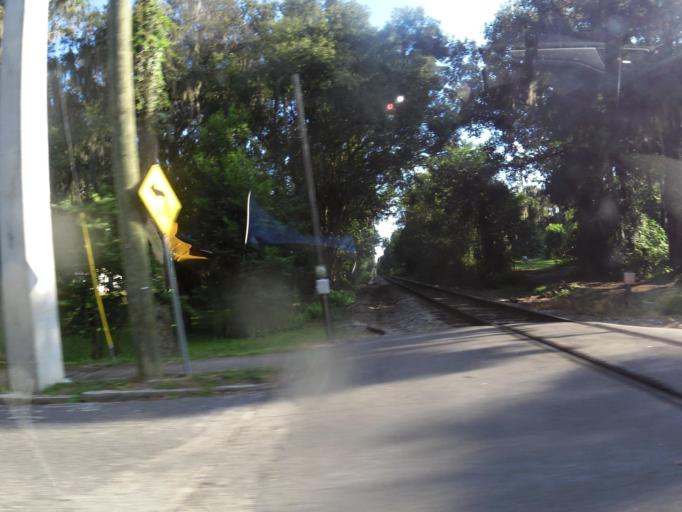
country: US
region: Florida
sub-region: Putnam County
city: Palatka
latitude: 29.6388
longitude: -81.6412
